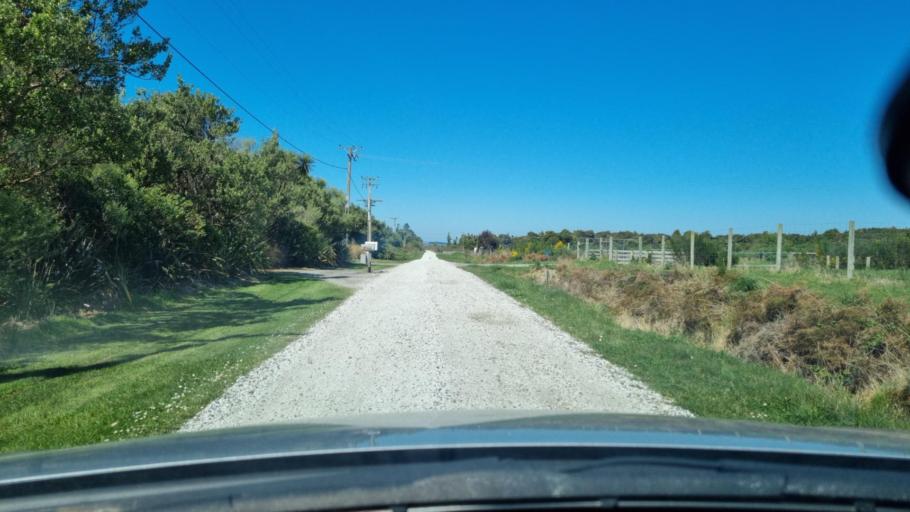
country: NZ
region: Southland
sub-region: Invercargill City
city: Invercargill
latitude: -46.4501
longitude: 168.3167
